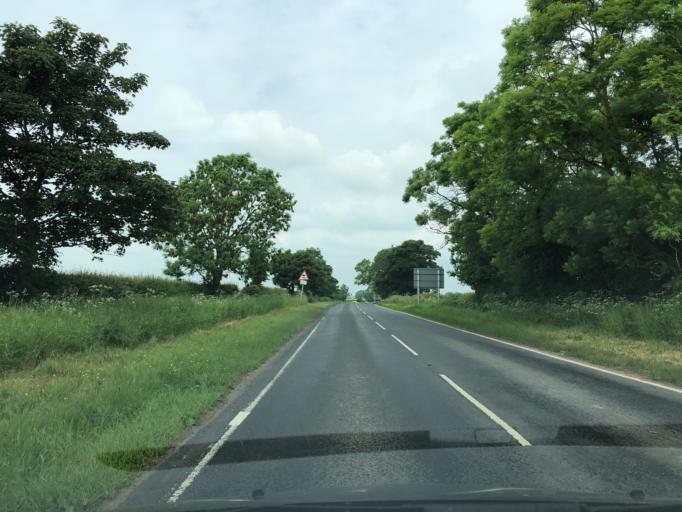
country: GB
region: England
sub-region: North Yorkshire
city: Thirsk
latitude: 54.2221
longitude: -1.4149
